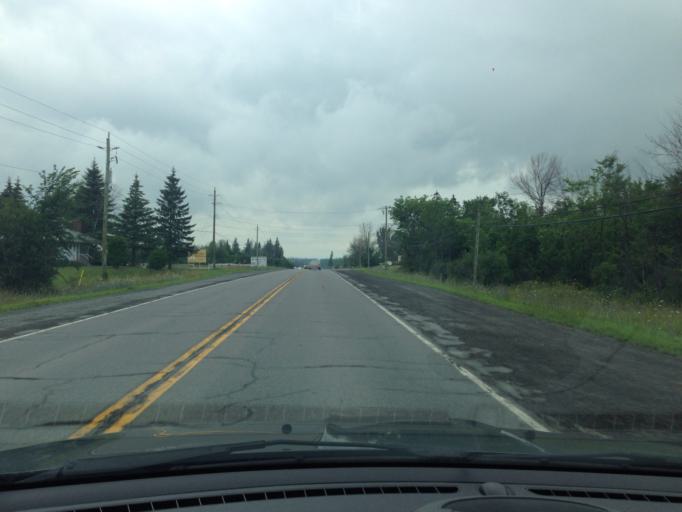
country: CA
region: Ontario
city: Ottawa
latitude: 45.2994
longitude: -75.5815
